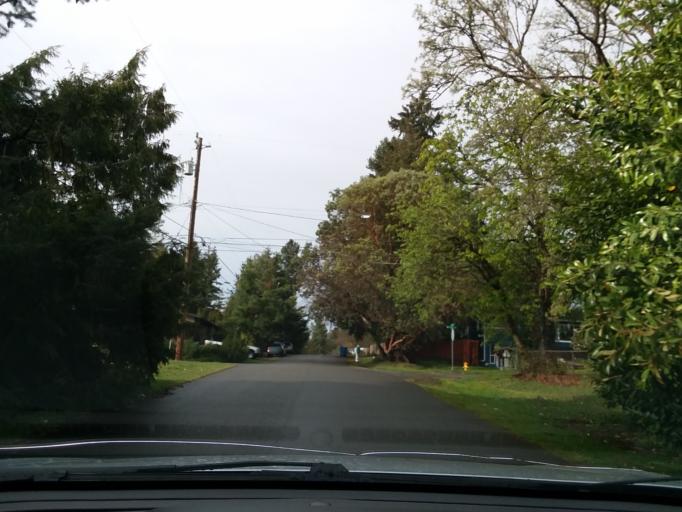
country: US
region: Washington
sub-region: King County
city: Shoreline
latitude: 47.7442
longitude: -122.3265
